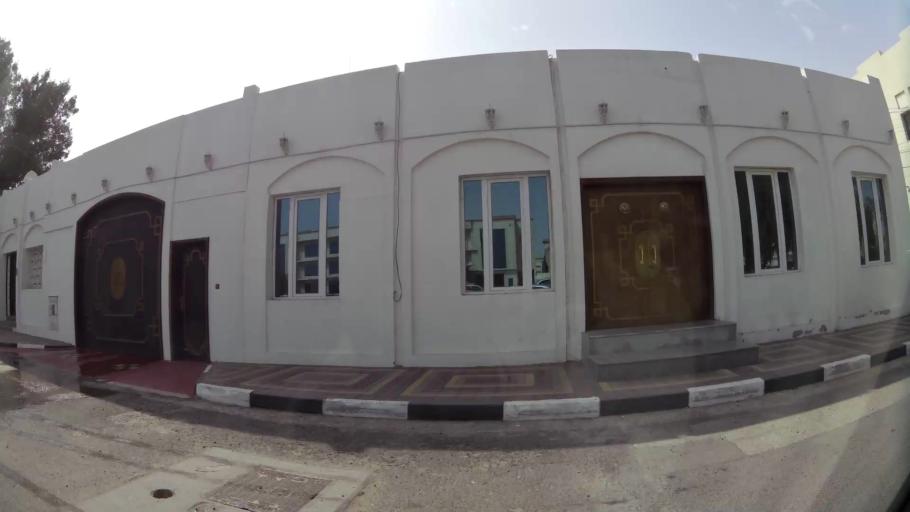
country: QA
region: Baladiyat ar Rayyan
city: Ar Rayyan
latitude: 25.3073
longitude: 51.4759
